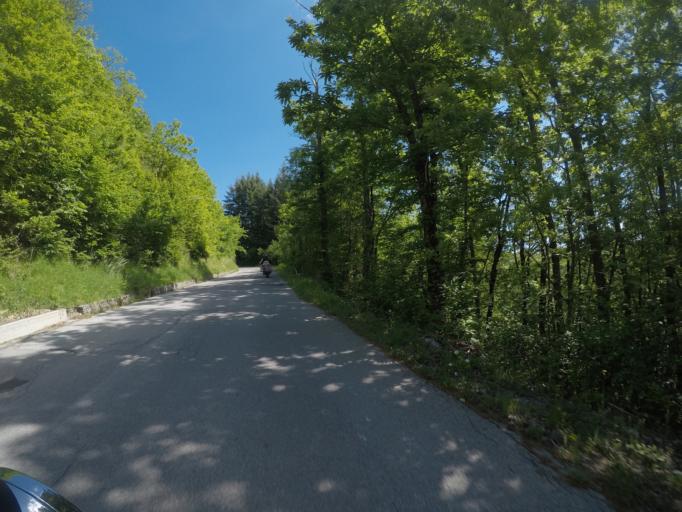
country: IT
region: Tuscany
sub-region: Provincia di Lucca
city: Careggine
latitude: 44.0966
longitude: 10.3267
